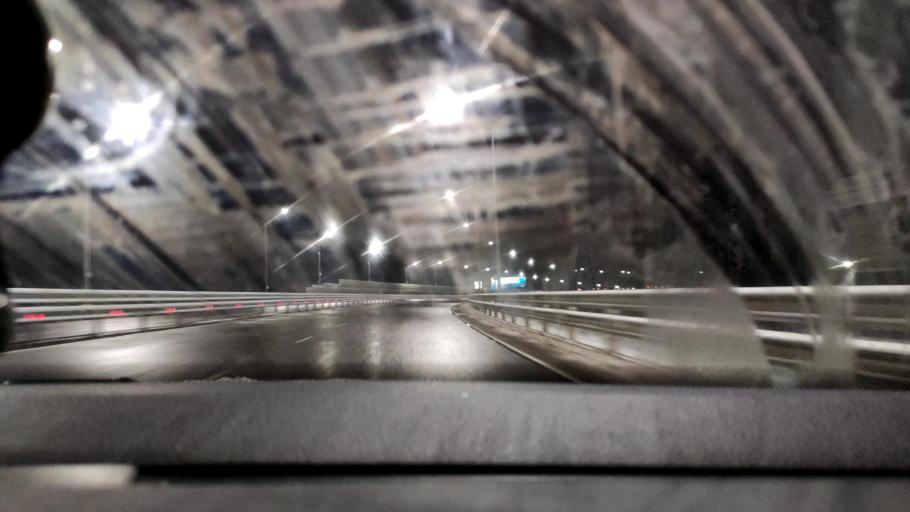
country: RU
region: Moskovskaya
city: Solnechnogorsk
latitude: 56.1643
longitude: 36.9186
